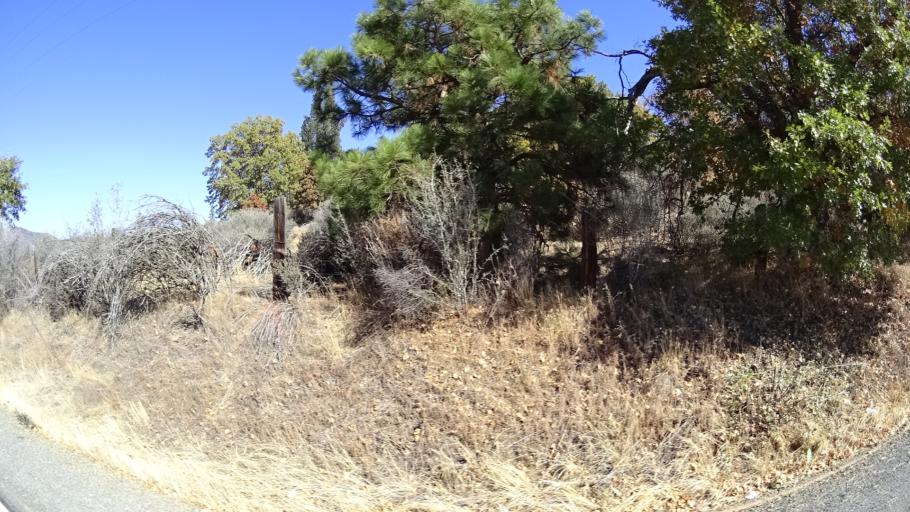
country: US
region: California
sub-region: Siskiyou County
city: Yreka
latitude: 41.5524
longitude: -122.9159
